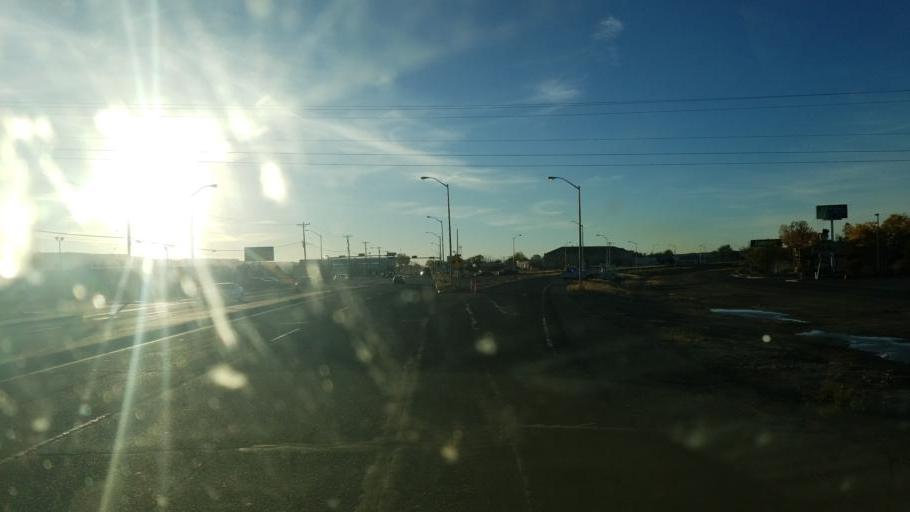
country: US
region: New Mexico
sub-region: San Juan County
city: Farmington
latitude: 36.7194
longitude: -108.1808
